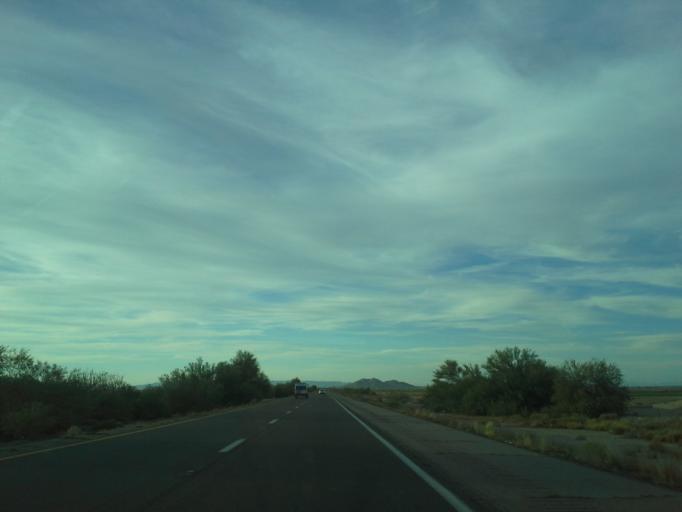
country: US
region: Arizona
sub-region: Pinal County
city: Sacaton
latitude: 33.0805
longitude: -111.8130
